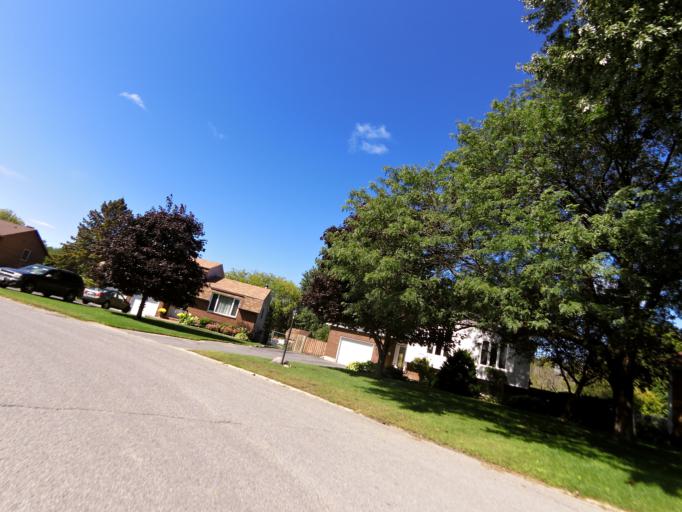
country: CA
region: Ontario
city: Bells Corners
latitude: 45.1951
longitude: -75.8273
